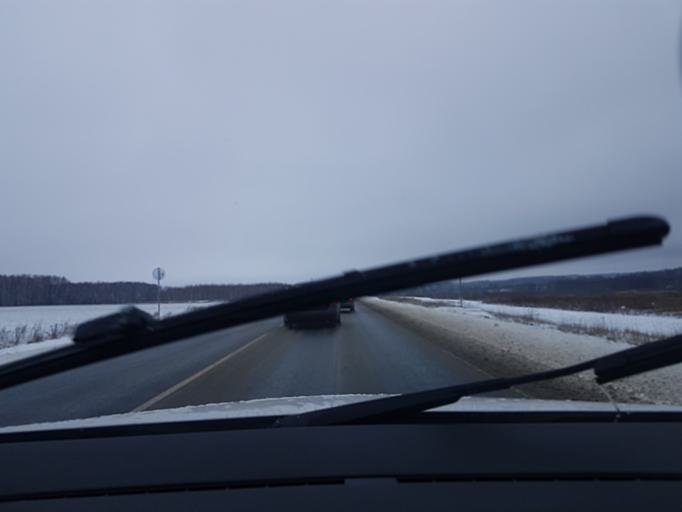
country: RU
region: Moskovskaya
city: Ozherel'ye
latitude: 54.6143
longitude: 38.3976
